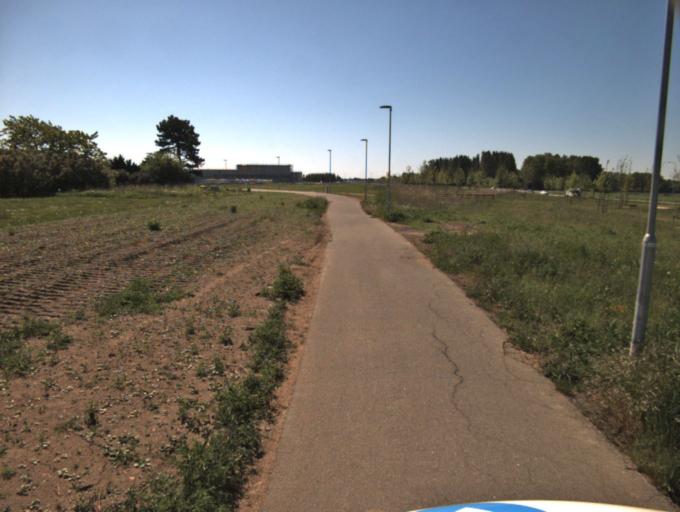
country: SE
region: Skane
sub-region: Kristianstads Kommun
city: Kristianstad
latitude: 56.0277
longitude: 14.1902
